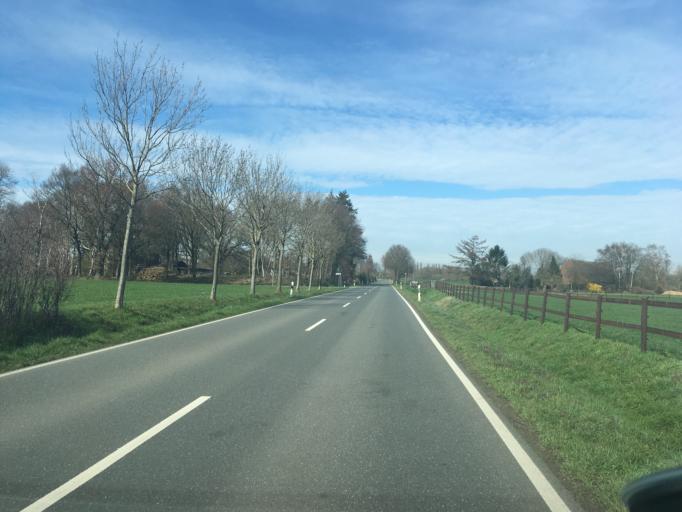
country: DE
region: North Rhine-Westphalia
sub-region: Regierungsbezirk Munster
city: Isselburg
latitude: 51.8471
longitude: 6.4775
